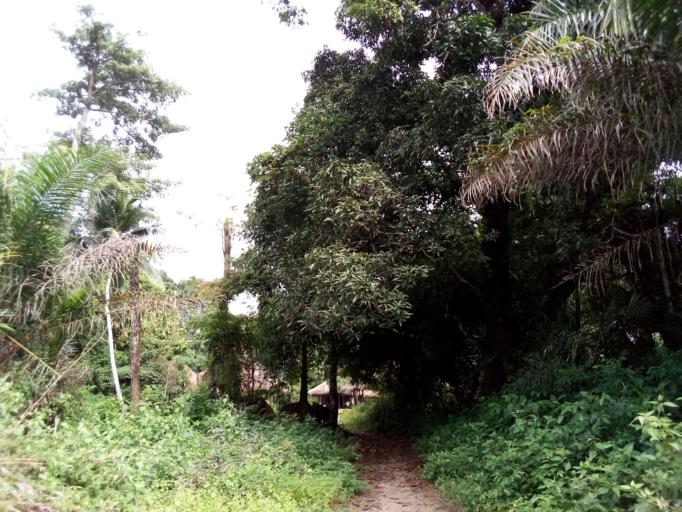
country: SL
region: Southern Province
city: Bonthe
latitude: 7.5104
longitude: -12.5532
